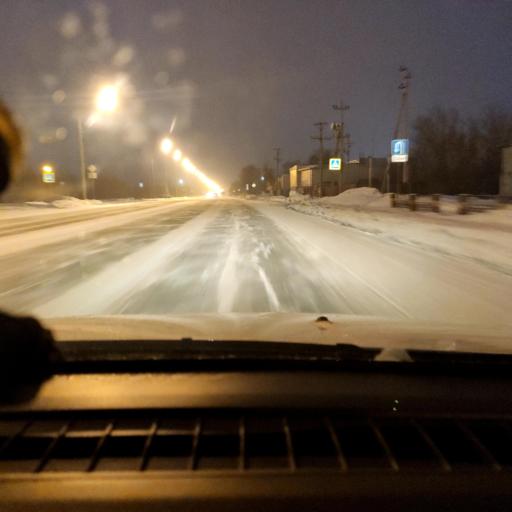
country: RU
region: Samara
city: Otradnyy
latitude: 53.3696
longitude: 51.3637
